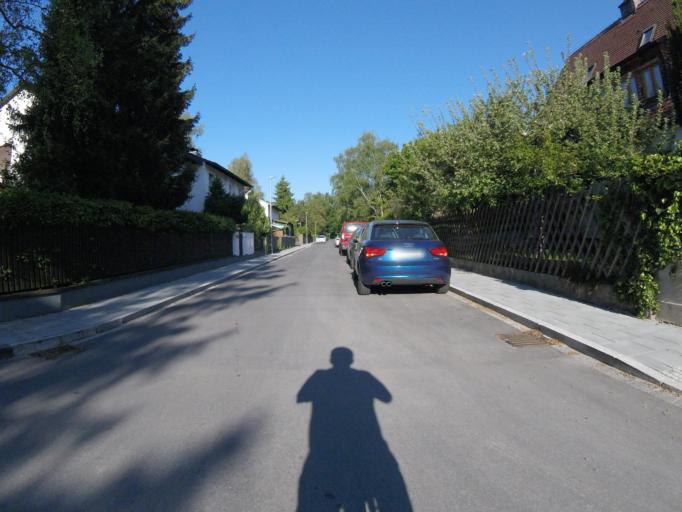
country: DE
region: Bavaria
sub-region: Upper Bavaria
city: Ottobrunn
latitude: 48.0628
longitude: 11.6596
